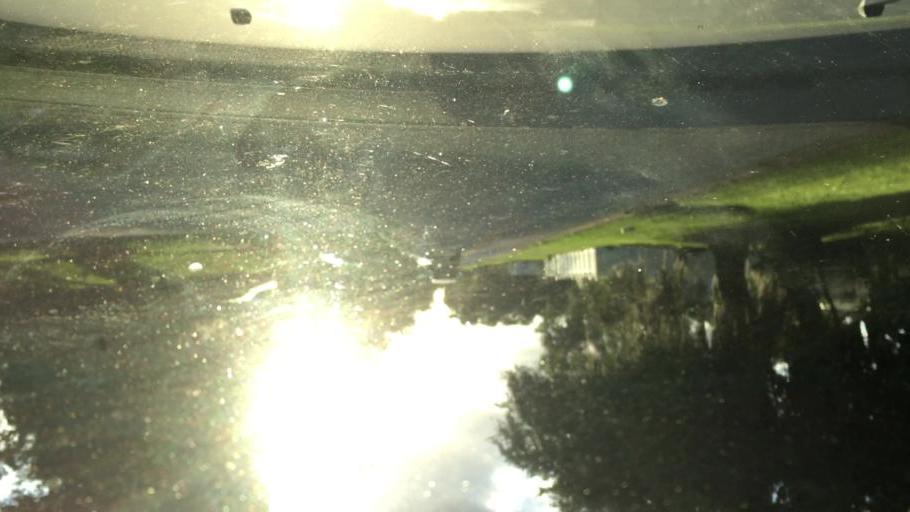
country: US
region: Florida
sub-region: Volusia County
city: Ormond Beach
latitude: 29.2634
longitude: -81.0668
